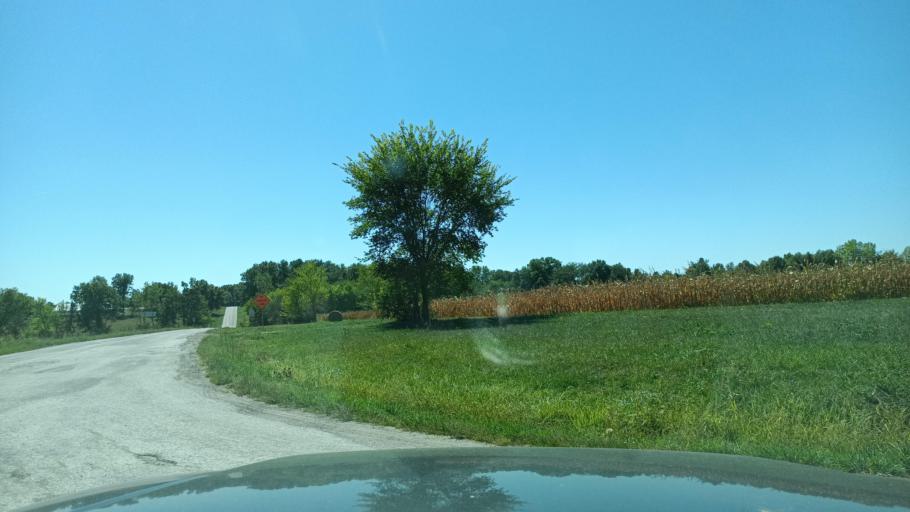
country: US
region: Missouri
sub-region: Macon County
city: La Plata
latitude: 40.0235
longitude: -92.6000
